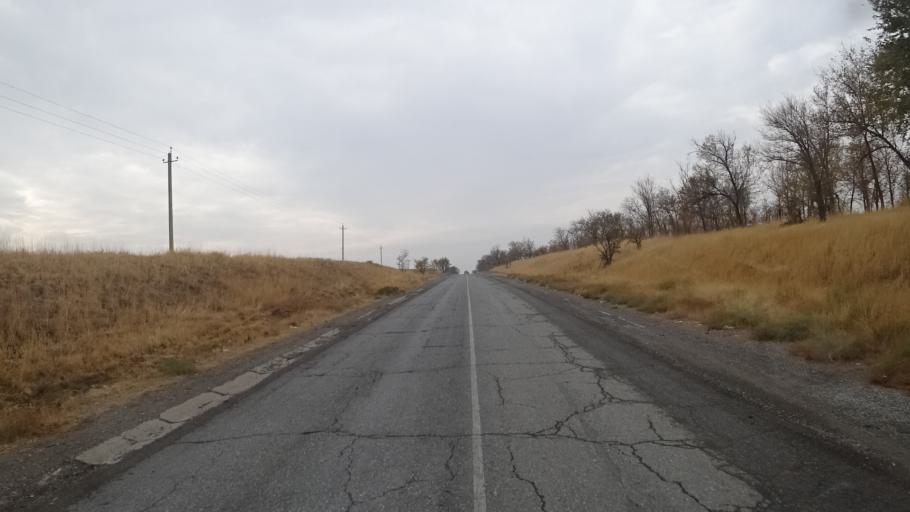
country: KZ
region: Ongtustik Qazaqstan
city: Aksu
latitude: 42.4189
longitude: 69.6892
